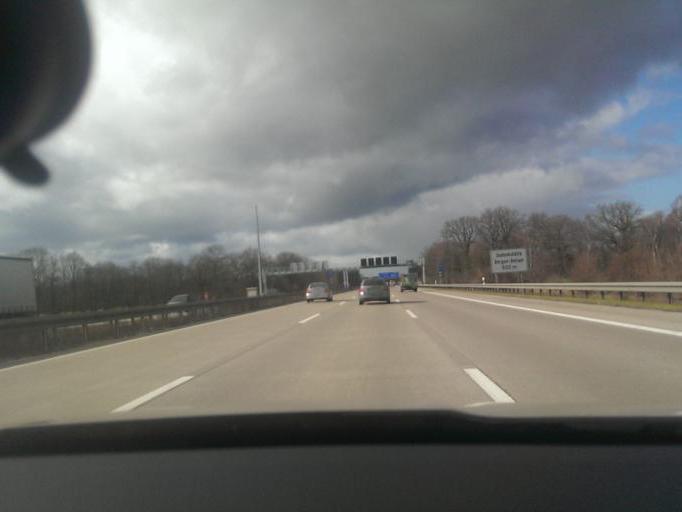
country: DE
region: Lower Saxony
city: Isernhagen Farster Bauerschaft
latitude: 52.5365
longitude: 9.8049
